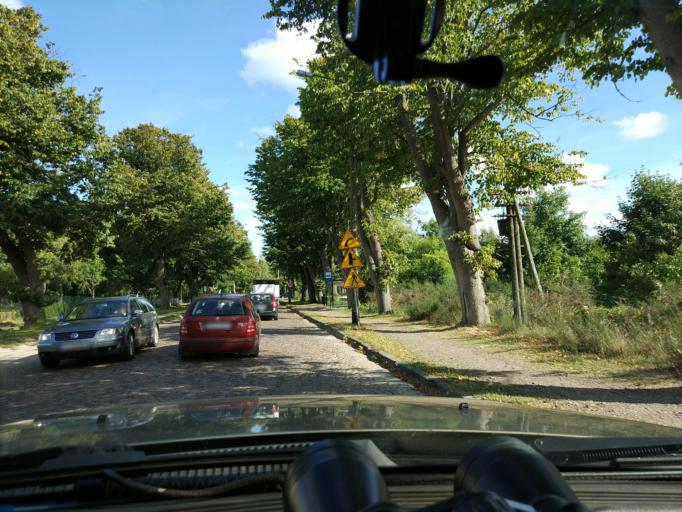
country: PL
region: Pomeranian Voivodeship
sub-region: Powiat pucki
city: Jastrzebia Gora
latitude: 54.8281
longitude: 18.3354
